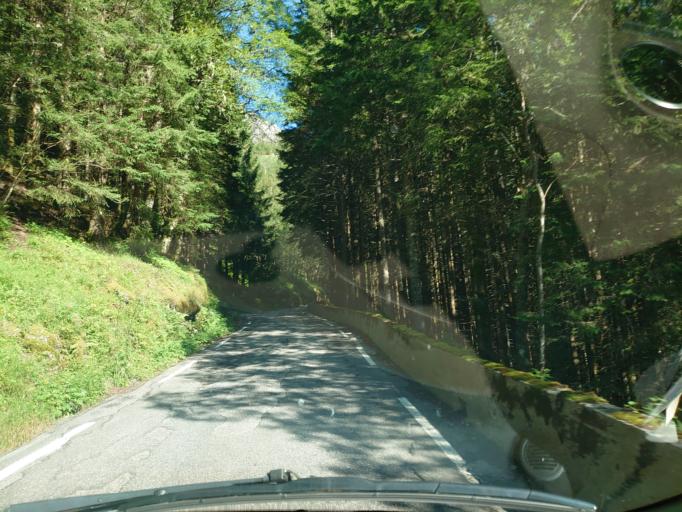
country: NO
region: Hordaland
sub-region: Vaksdal
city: Dale
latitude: 60.5804
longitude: 5.8614
